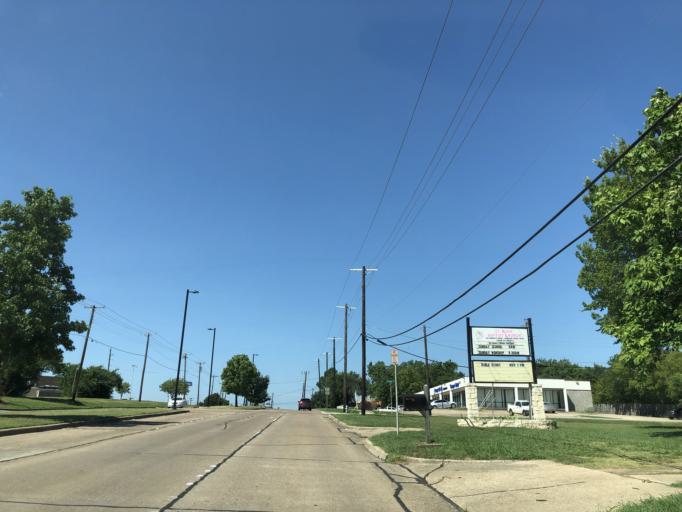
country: US
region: Texas
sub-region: Dallas County
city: Sunnyvale
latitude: 32.8481
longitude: -96.5932
